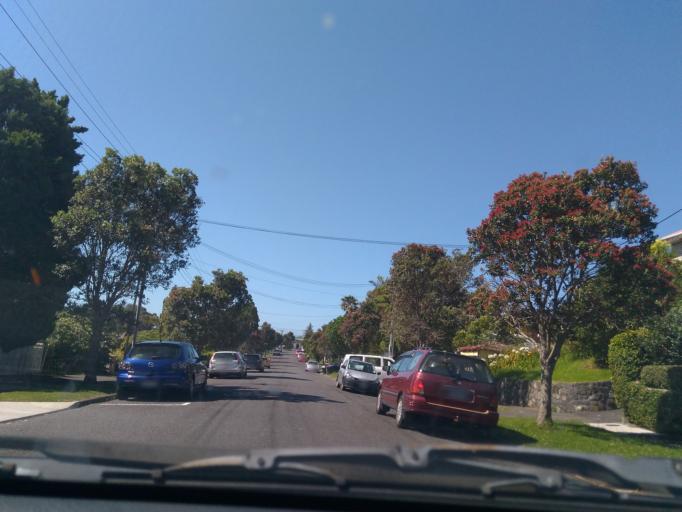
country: NZ
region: Auckland
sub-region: Auckland
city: Rosebank
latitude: -36.8824
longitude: 174.6965
